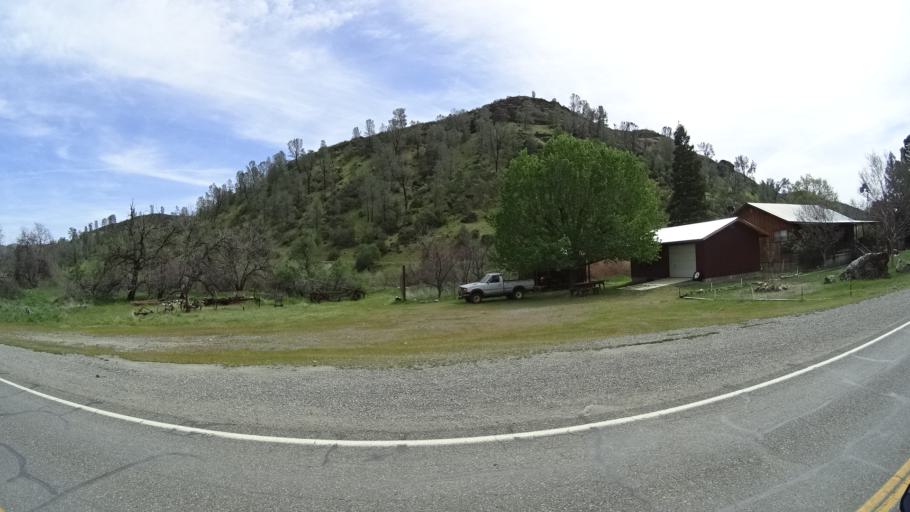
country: US
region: California
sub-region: Glenn County
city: Willows
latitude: 39.6043
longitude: -122.5371
